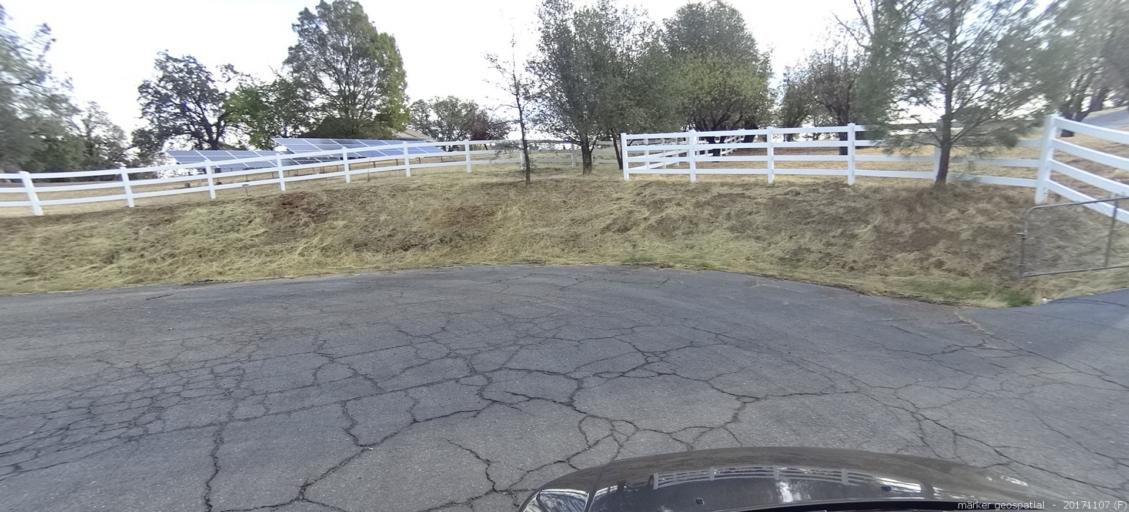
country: US
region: California
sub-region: Shasta County
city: Shasta
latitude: 40.5507
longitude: -122.4724
